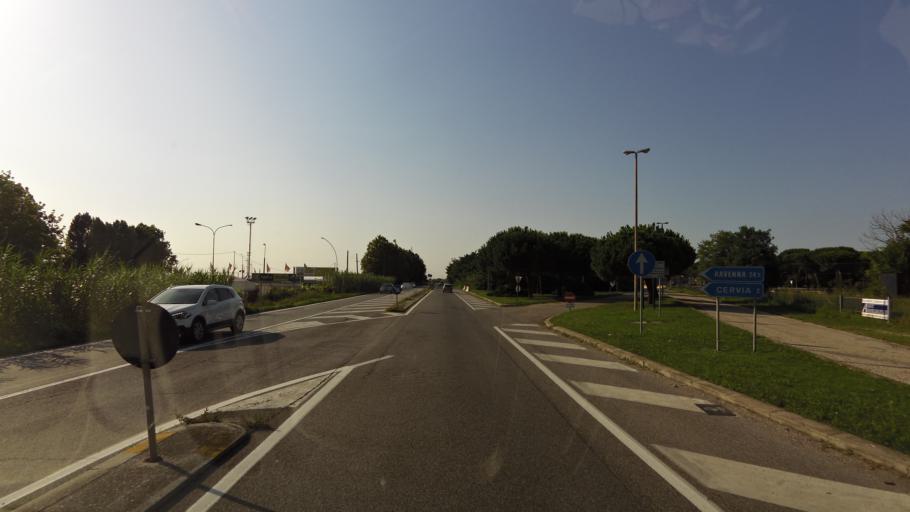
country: IT
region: Emilia-Romagna
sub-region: Provincia di Ravenna
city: Cervia
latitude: 44.2370
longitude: 12.3573
